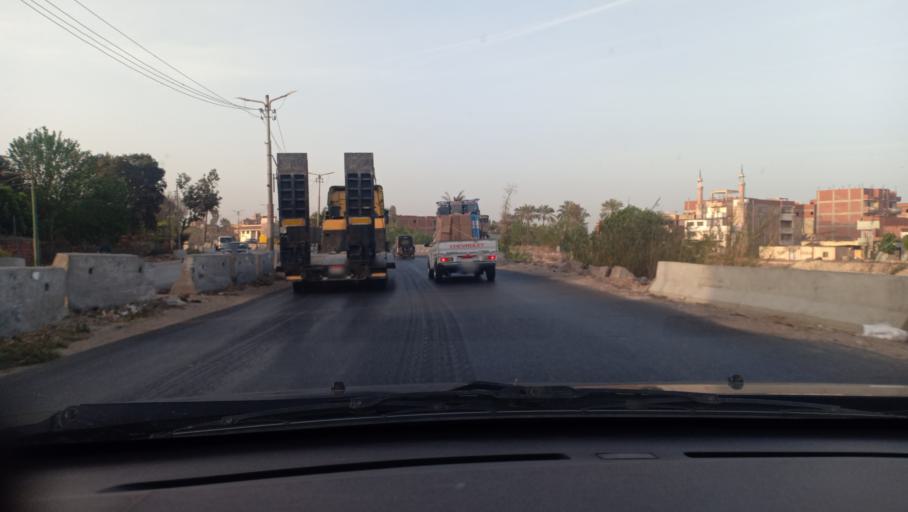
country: EG
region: Muhafazat al Minufiyah
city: Quwaysina
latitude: 30.5403
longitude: 31.2688
